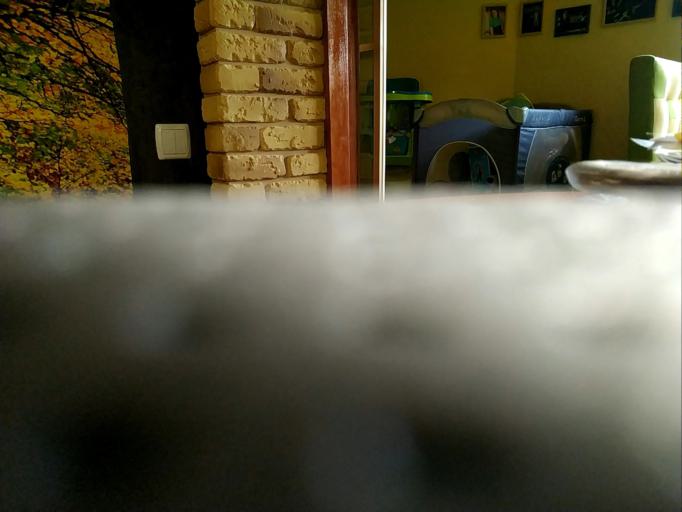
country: RU
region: Kaluga
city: Seredeyskiy
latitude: 53.9018
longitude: 35.3548
